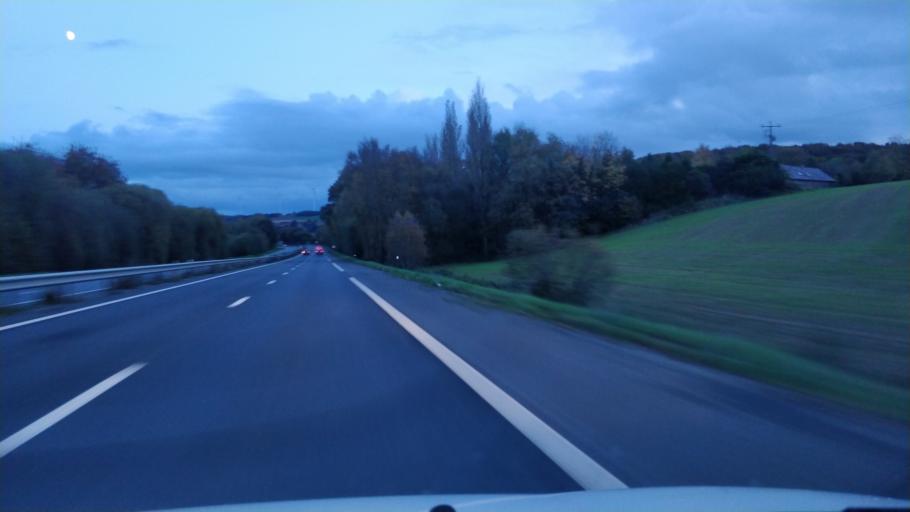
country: FR
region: Brittany
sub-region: Departement des Cotes-d'Armor
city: Plemet
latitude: 48.1726
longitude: -2.6530
